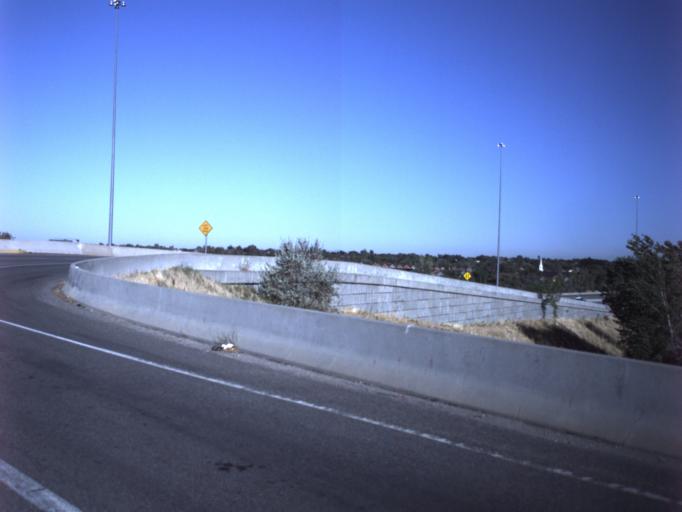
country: US
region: Utah
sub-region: Davis County
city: Farmington
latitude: 40.9914
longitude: -111.9017
